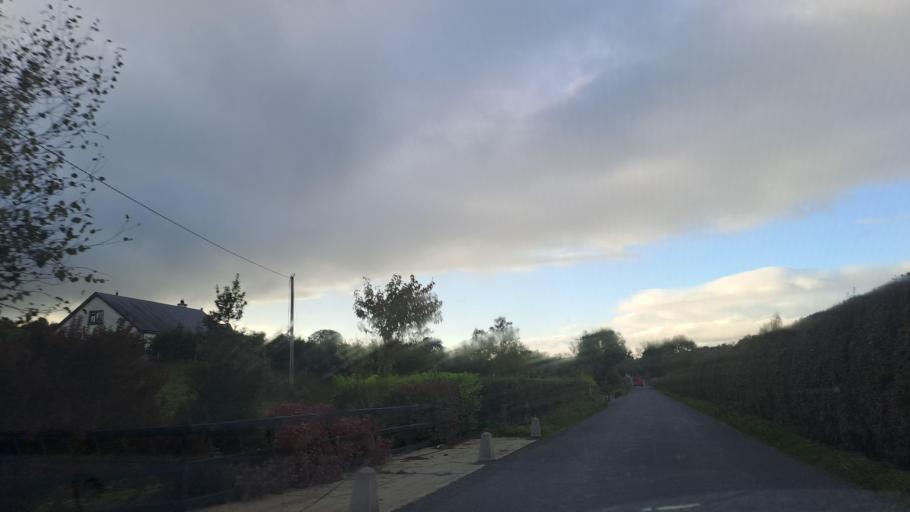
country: IE
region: Ulster
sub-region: County Monaghan
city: Carrickmacross
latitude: 54.0348
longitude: -6.8150
